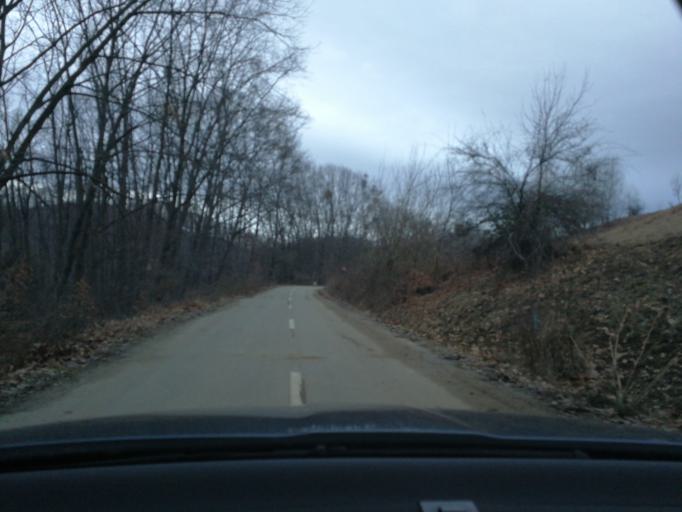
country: RO
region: Prahova
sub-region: Comuna Adunati
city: Ocina de Sus
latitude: 45.1749
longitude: 25.5713
